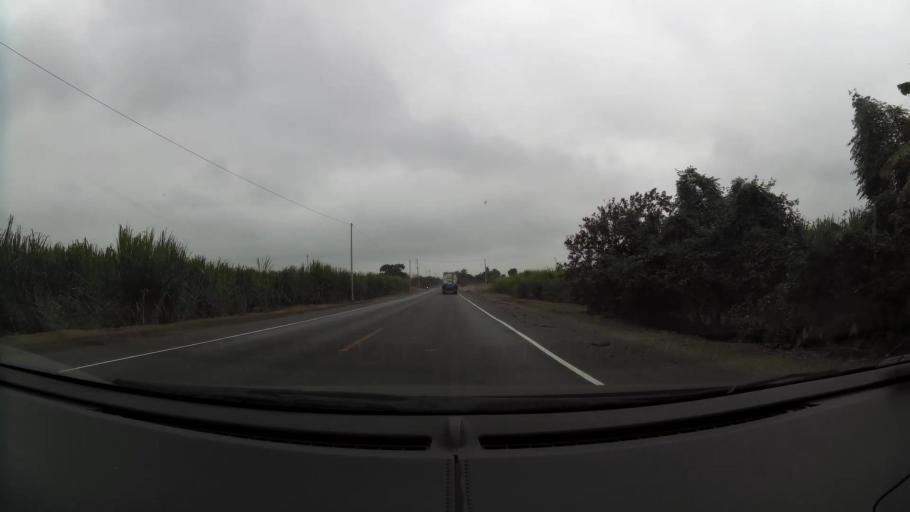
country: PE
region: La Libertad
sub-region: Viru
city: Viru
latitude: -8.4375
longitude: -78.7608
